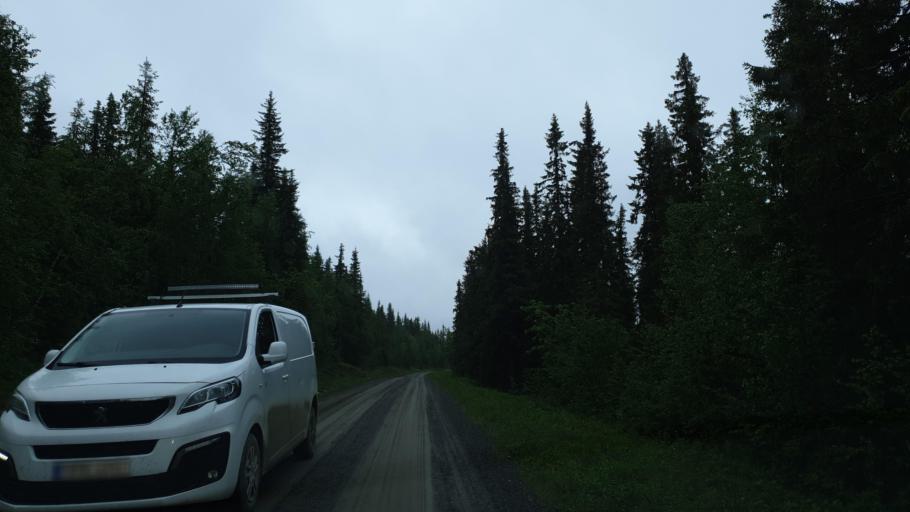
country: SE
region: Vaesterbotten
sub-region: Vilhelmina Kommun
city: Sjoberg
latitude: 65.3302
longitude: 15.9108
